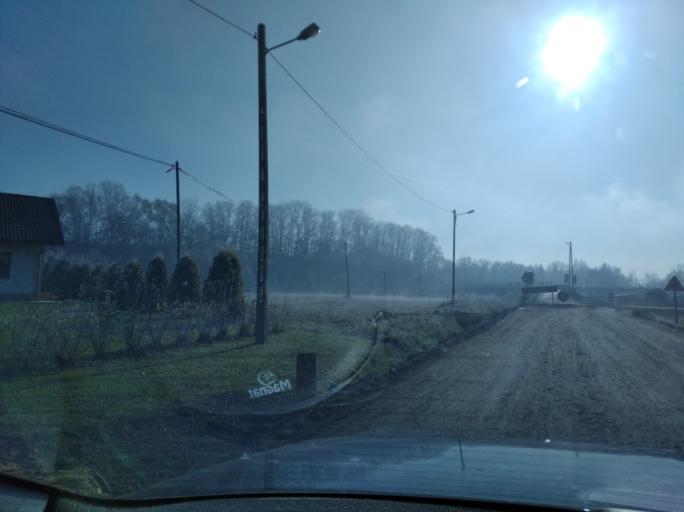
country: PL
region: Subcarpathian Voivodeship
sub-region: Powiat strzyzowski
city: Wysoka Strzyzowska
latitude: 49.8661
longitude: 21.7068
